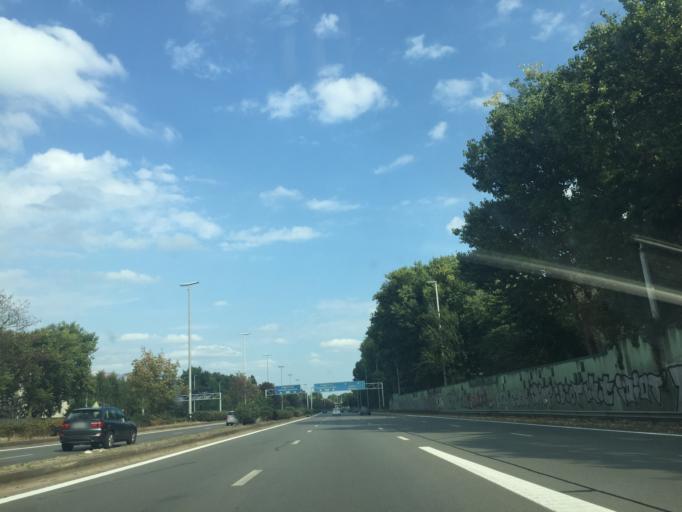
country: BE
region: Flanders
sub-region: Provincie Vlaams-Brabant
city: Diegem
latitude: 50.8545
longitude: 4.4178
